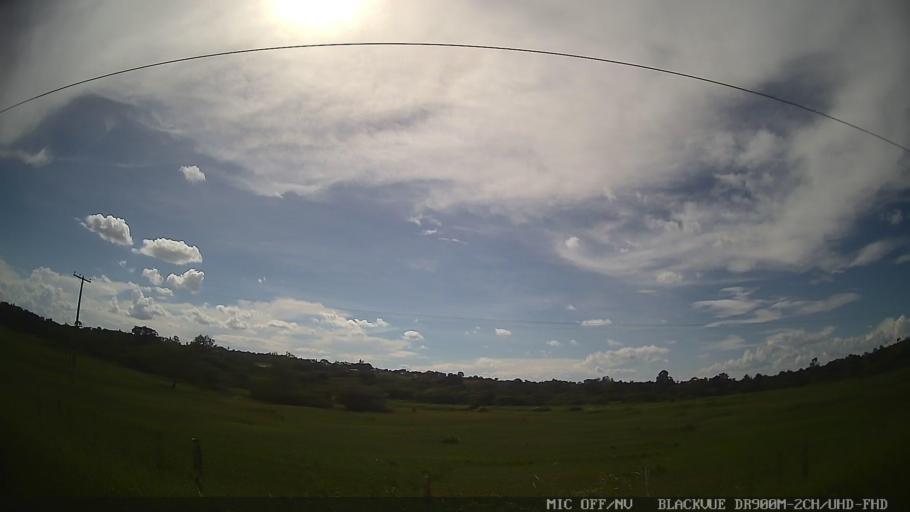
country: BR
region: Sao Paulo
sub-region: Conchas
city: Conchas
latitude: -23.0040
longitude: -48.0018
